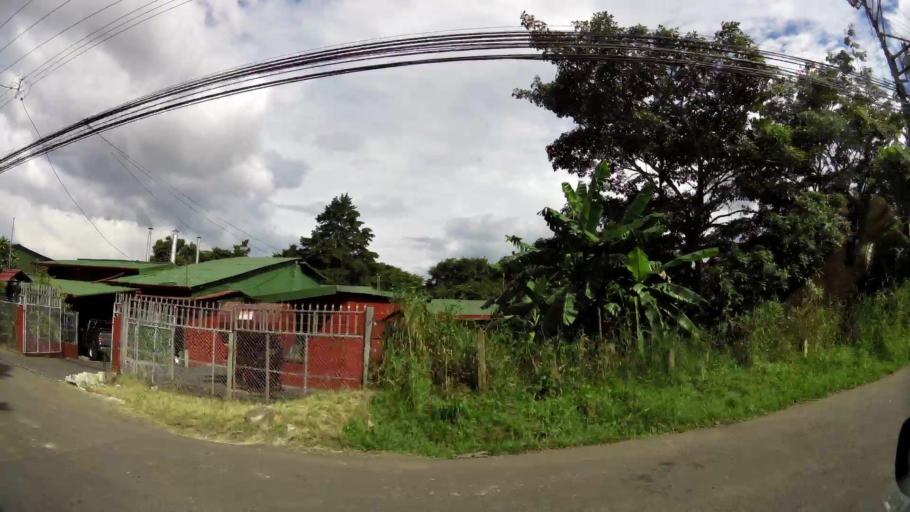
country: CR
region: San Jose
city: San Rafael Arriba
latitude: 9.8806
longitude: -84.0766
